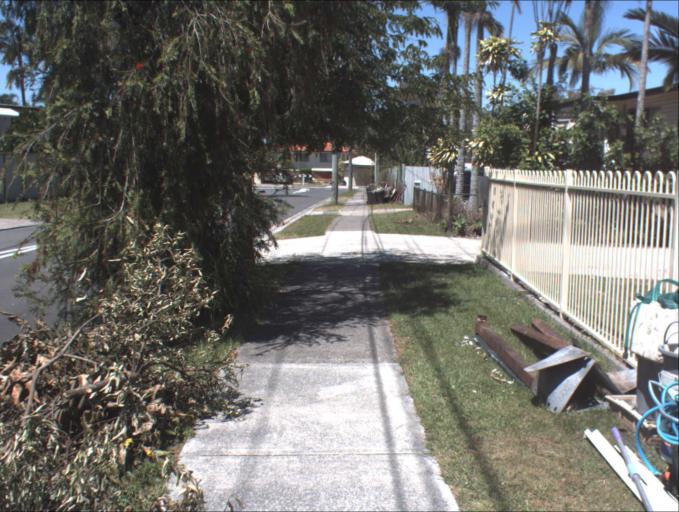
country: AU
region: Queensland
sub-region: Logan
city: Logan City
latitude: -27.6411
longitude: 153.1197
